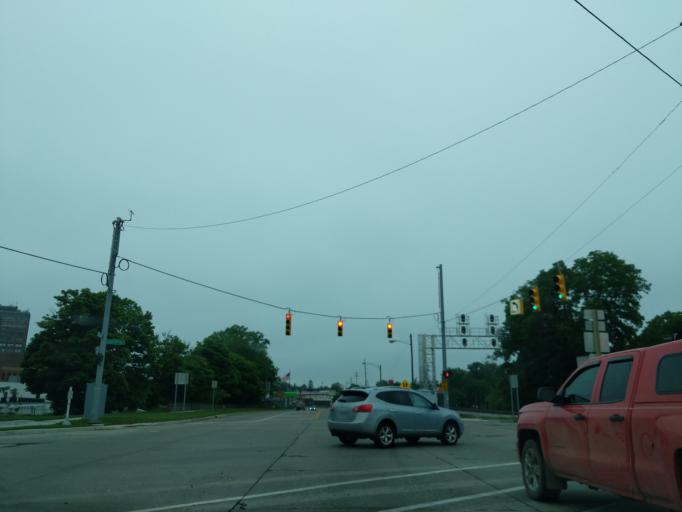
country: US
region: Michigan
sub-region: Jackson County
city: Jackson
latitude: 42.2485
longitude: -84.4031
